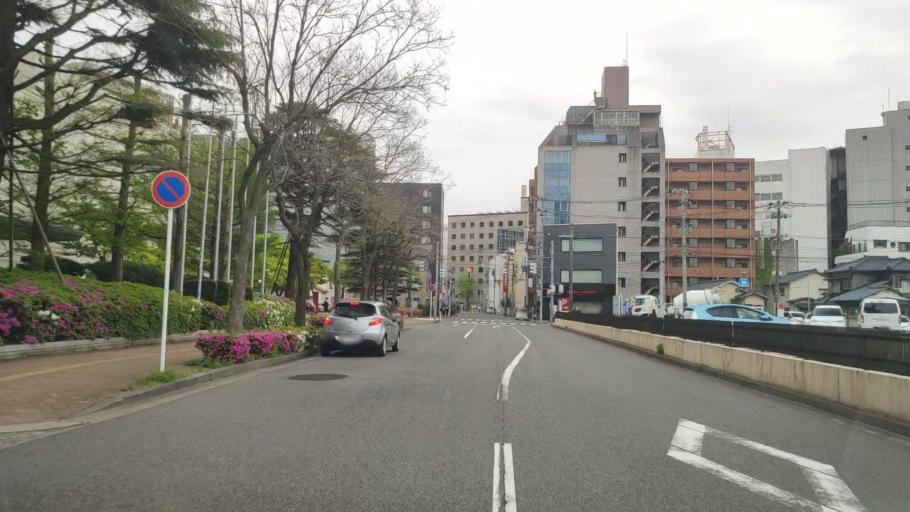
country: JP
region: Niigata
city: Niigata-shi
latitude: 37.9188
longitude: 139.0586
